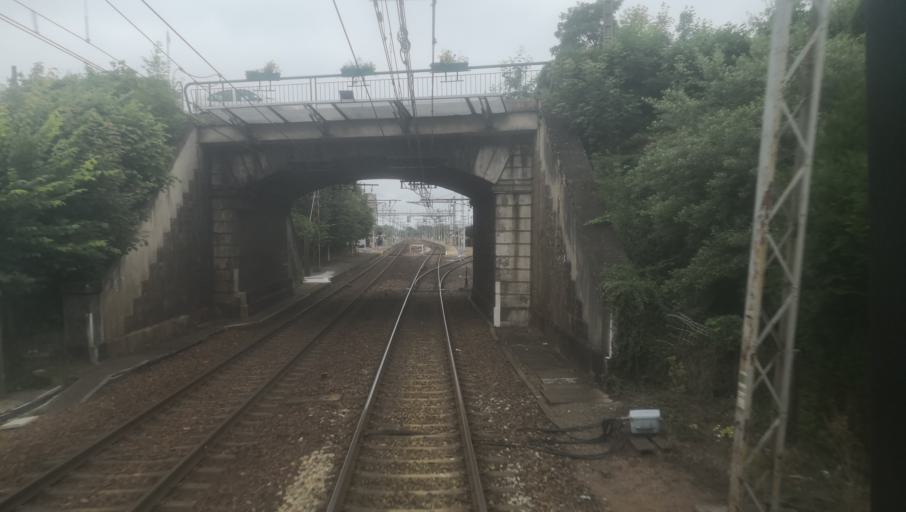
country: FR
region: Limousin
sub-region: Departement de la Creuse
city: La Souterraine
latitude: 46.2384
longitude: 1.4936
